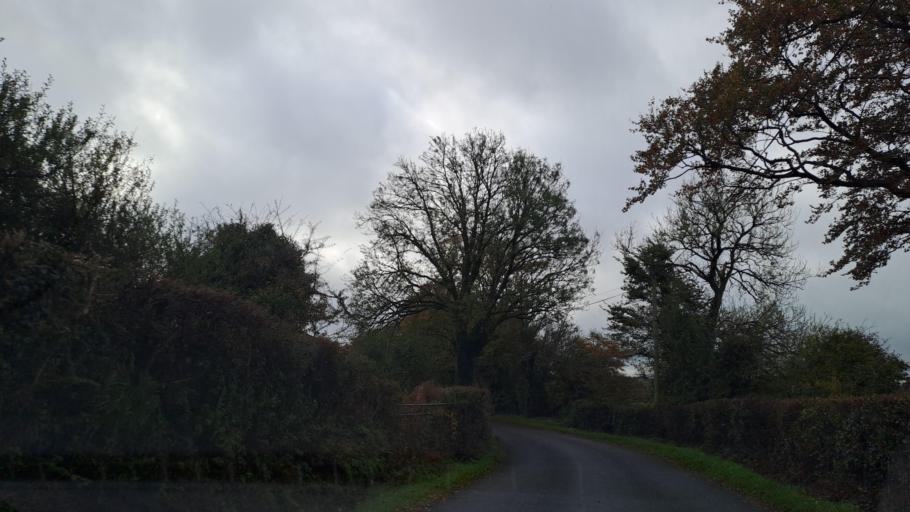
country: IE
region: Ulster
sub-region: An Cabhan
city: Bailieborough
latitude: 53.9332
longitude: -6.9747
